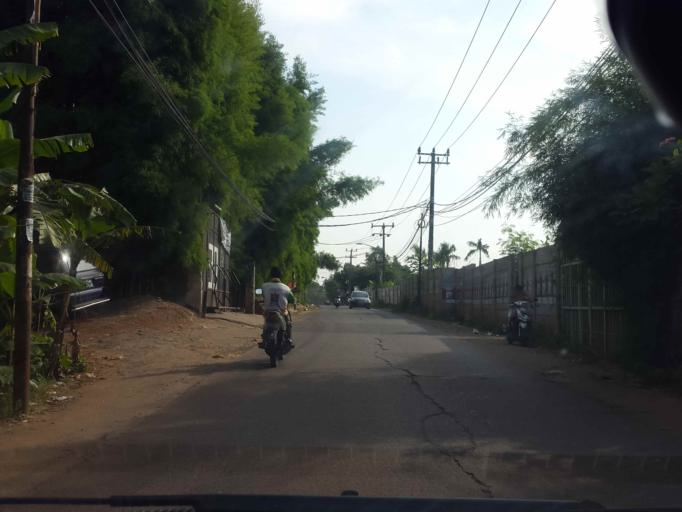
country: ID
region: West Java
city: Ciputat
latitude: -6.2678
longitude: 106.6714
